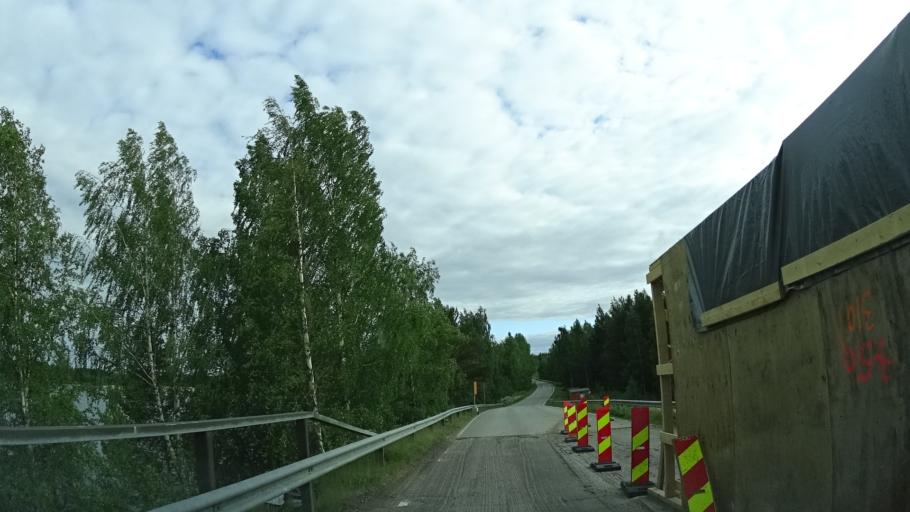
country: FI
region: Paijanne Tavastia
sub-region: Lahti
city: Sysmae
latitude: 61.6162
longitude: 25.6643
